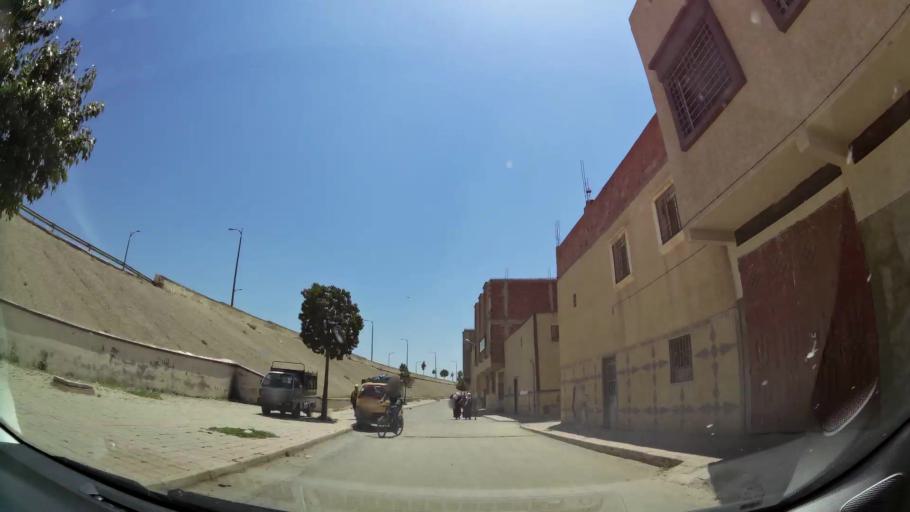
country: MA
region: Oriental
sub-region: Oujda-Angad
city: Oujda
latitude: 34.6937
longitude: -1.9427
